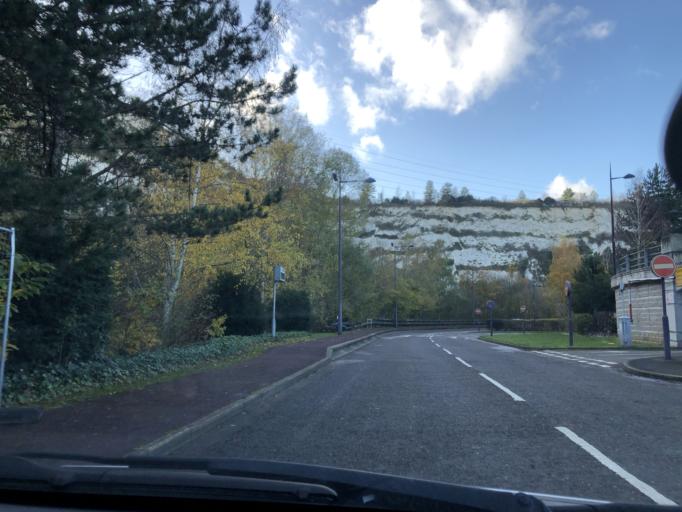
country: GB
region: England
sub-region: Kent
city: Stone
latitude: 51.4372
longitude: 0.2663
